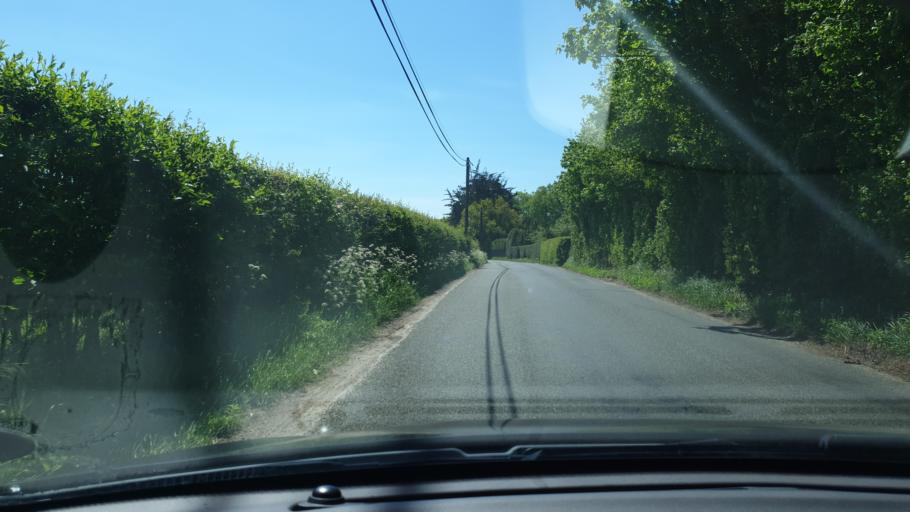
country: GB
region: England
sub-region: Essex
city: Great Bentley
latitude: 51.8762
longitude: 1.0818
